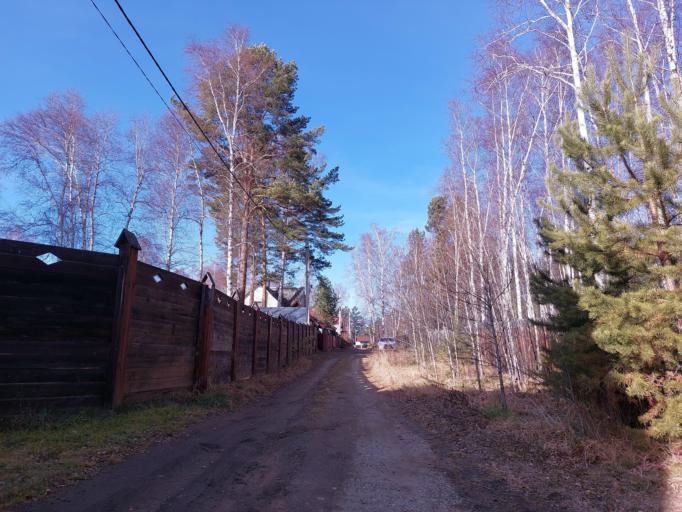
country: RU
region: Irkutsk
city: Pivovarikha
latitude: 52.1863
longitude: 104.4554
